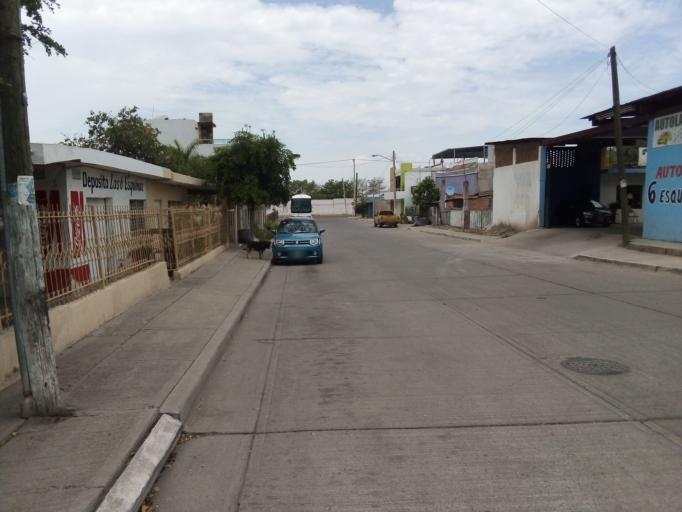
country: MX
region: Sinaloa
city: Culiacan
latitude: 24.7719
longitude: -107.4306
